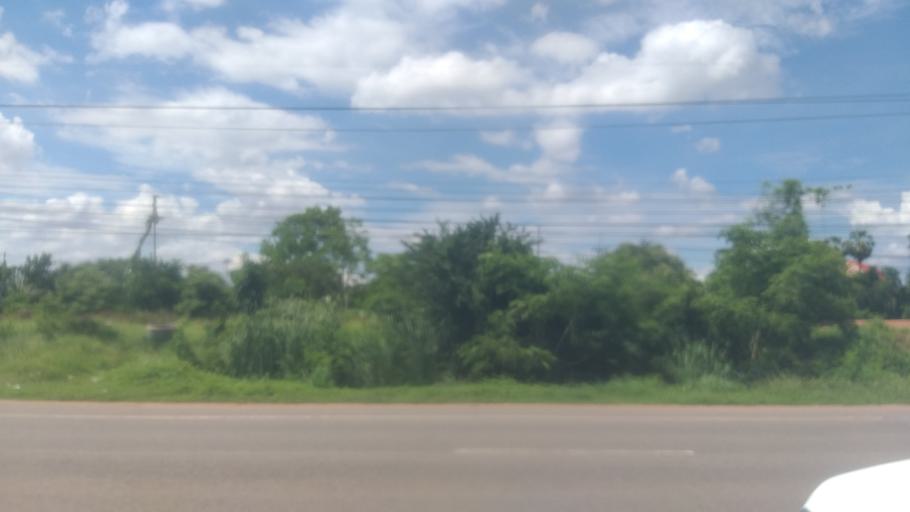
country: TH
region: Nakhon Ratchasima
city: Phra Thong Kham
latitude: 15.3076
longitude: 101.9703
